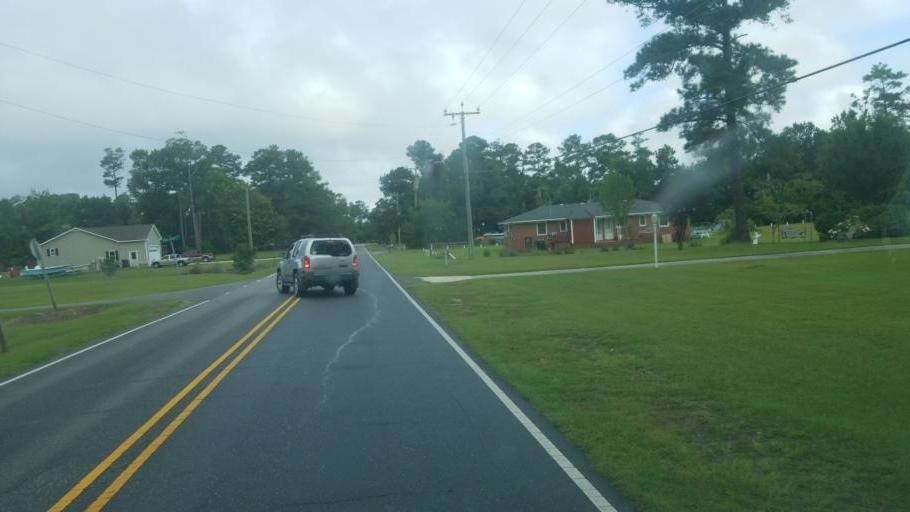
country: US
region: North Carolina
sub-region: Dare County
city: Wanchese
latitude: 35.8473
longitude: -75.6392
